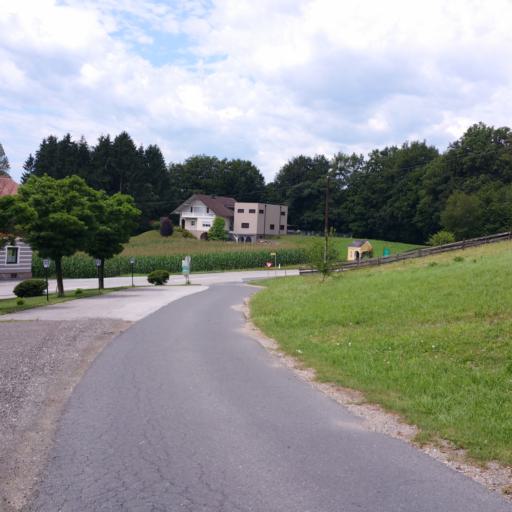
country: AT
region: Styria
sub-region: Politischer Bezirk Leibnitz
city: Gleinstatten
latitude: 46.7410
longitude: 15.3689
